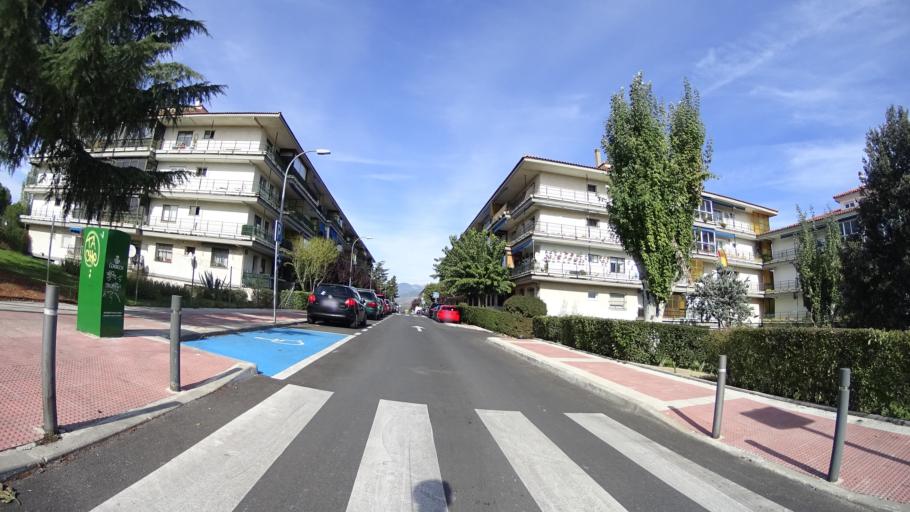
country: ES
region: Madrid
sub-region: Provincia de Madrid
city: Collado-Villalba
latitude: 40.6170
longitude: -4.0117
